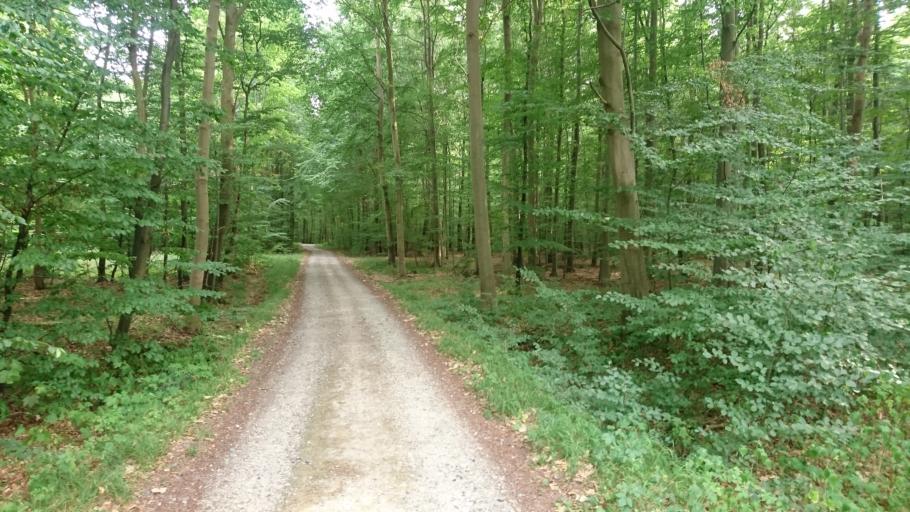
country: DK
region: Zealand
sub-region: Vordingborg Kommune
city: Stege
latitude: 54.9068
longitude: 12.2305
